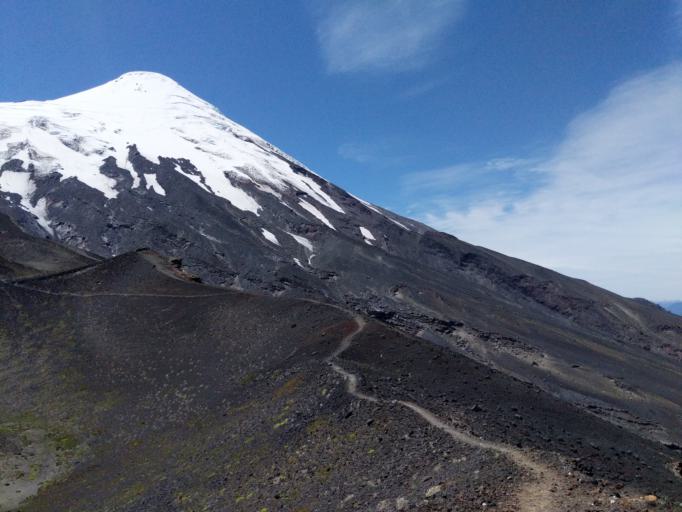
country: CL
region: Los Lagos
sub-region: Provincia de Llanquihue
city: La Ensenada
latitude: -41.1286
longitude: -72.5197
